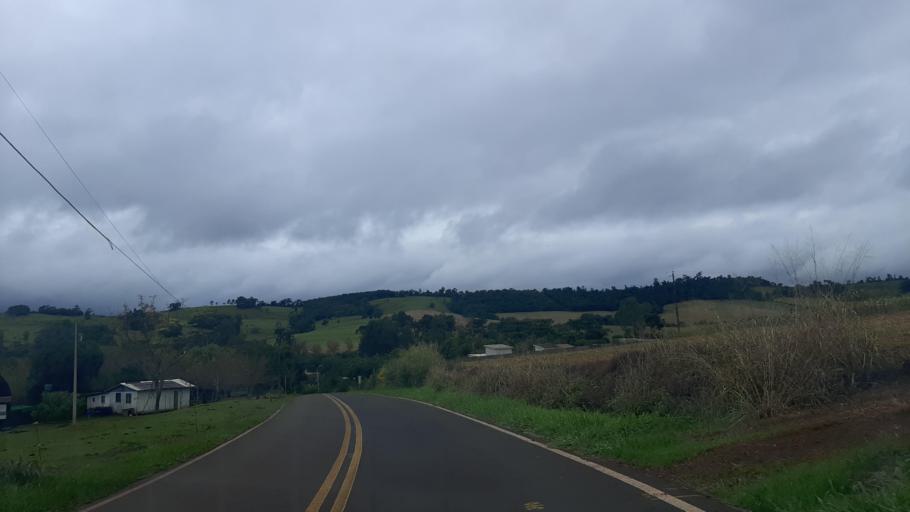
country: BR
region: Parana
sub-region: Ampere
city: Ampere
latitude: -25.9735
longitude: -53.4439
